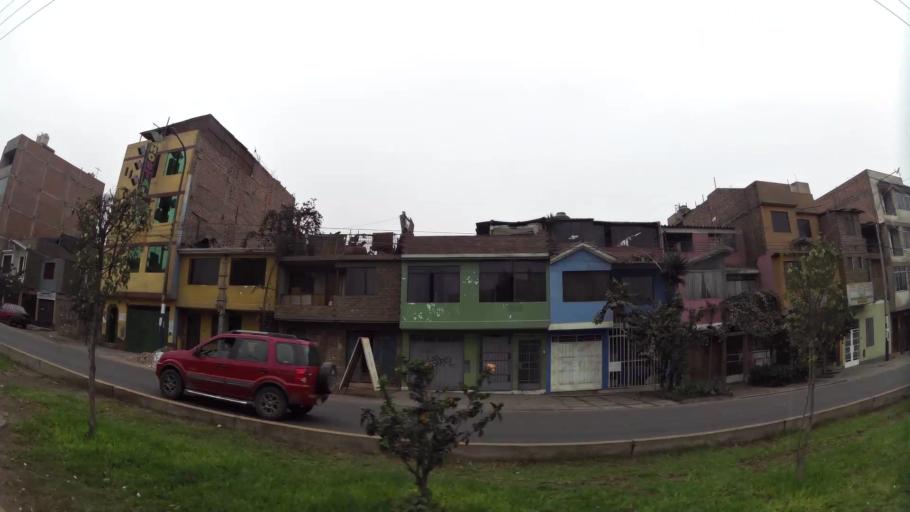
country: PE
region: Lima
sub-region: Lima
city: Independencia
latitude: -11.9576
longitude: -76.9830
